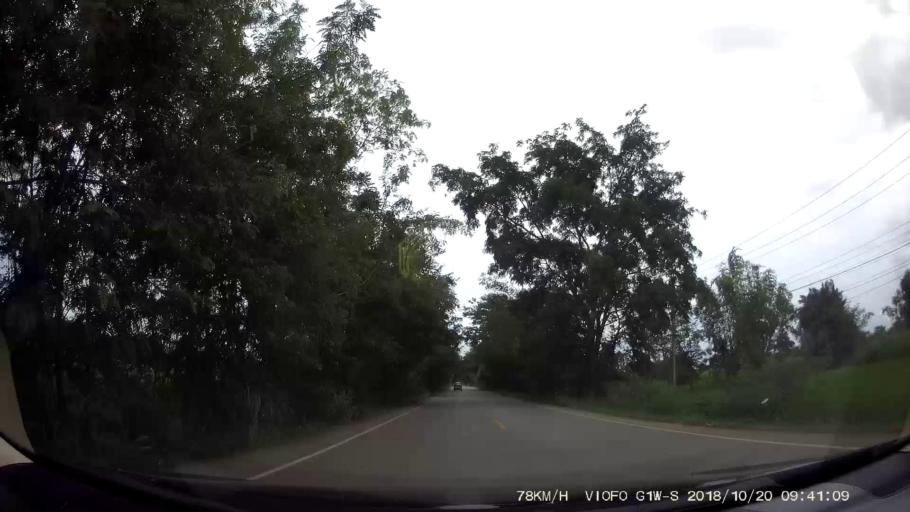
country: TH
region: Chaiyaphum
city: Khon San
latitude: 16.4504
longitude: 101.9582
